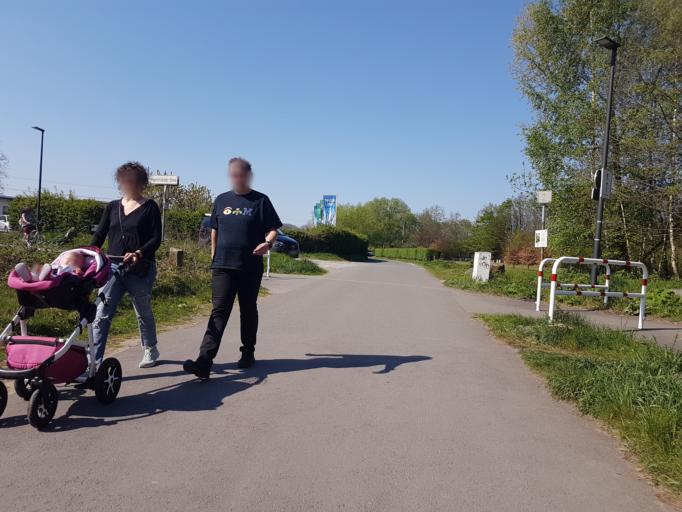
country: DE
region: North Rhine-Westphalia
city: Witten
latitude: 51.4277
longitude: 7.2900
